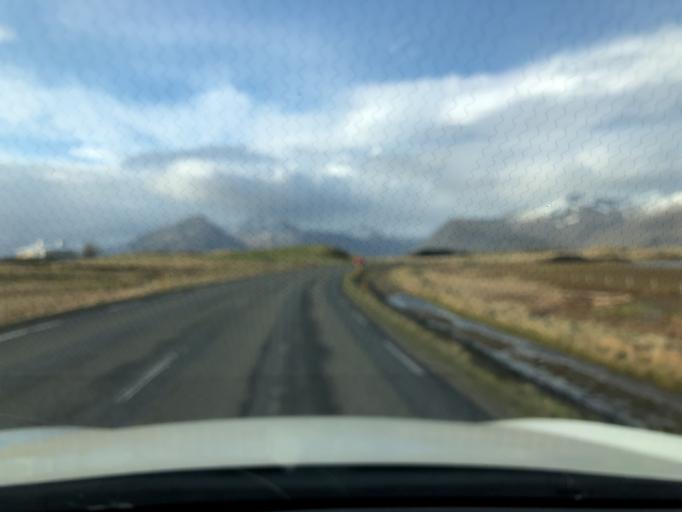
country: IS
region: East
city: Hoefn
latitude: 64.2737
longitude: -15.2023
